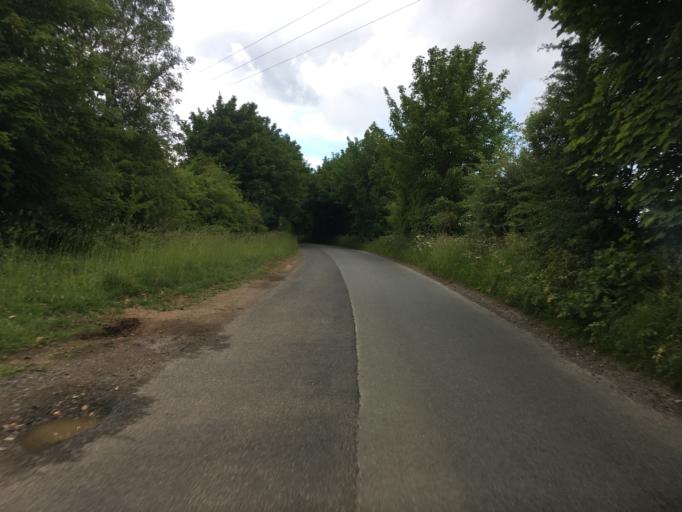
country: GB
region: England
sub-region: Gloucestershire
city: Coates
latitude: 51.7562
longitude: -2.0590
